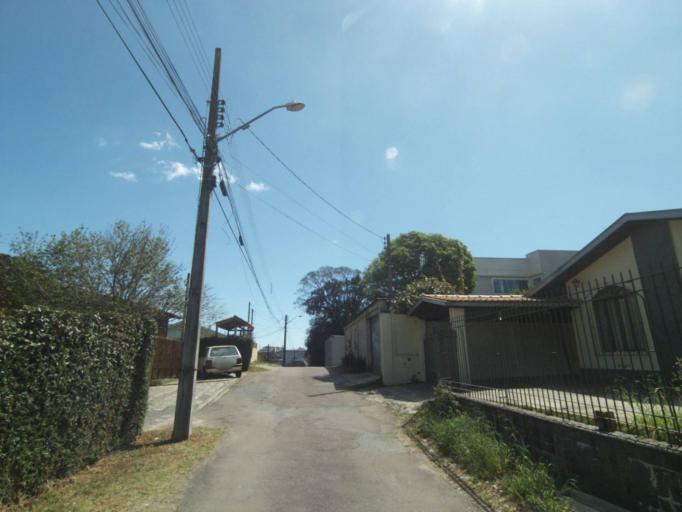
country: BR
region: Parana
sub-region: Curitiba
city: Curitiba
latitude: -25.3837
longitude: -49.2584
